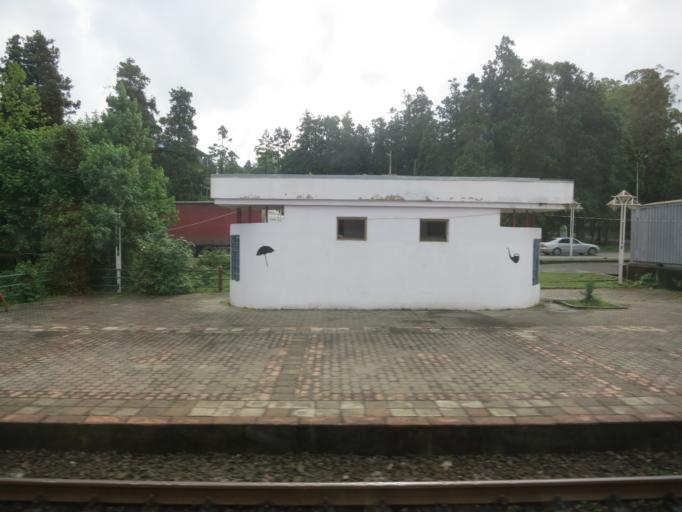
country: GE
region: Guria
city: Urek'i
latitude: 41.9985
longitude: 41.7798
